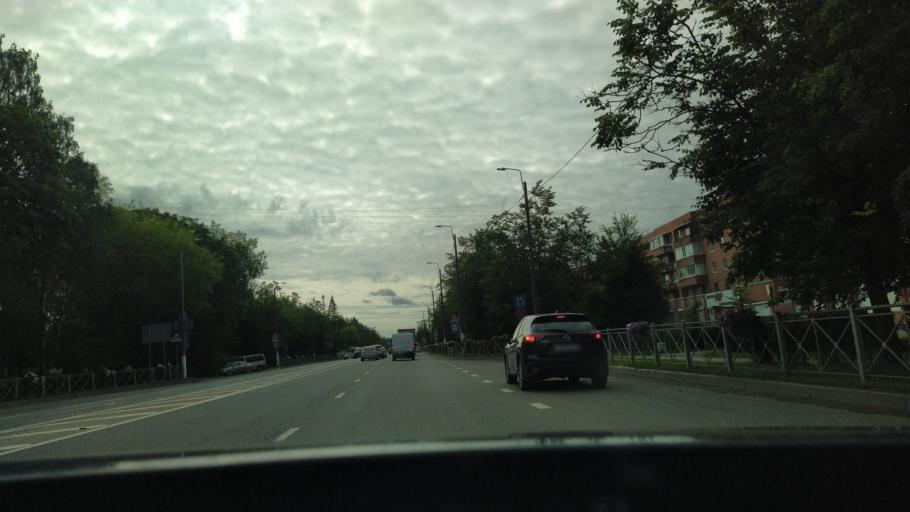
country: RU
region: Leningrad
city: Tosno
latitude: 59.5448
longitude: 30.8698
